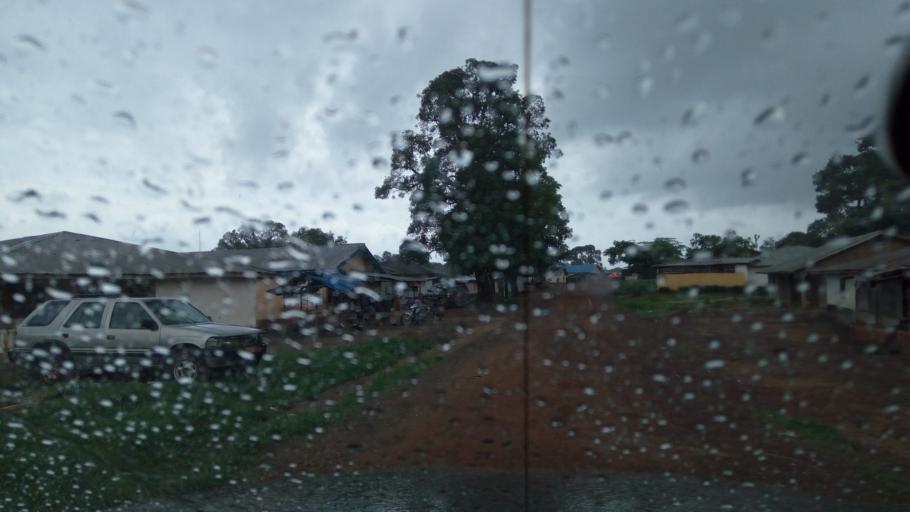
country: SL
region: Southern Province
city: Gandorhun
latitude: 7.4336
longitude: -11.8408
